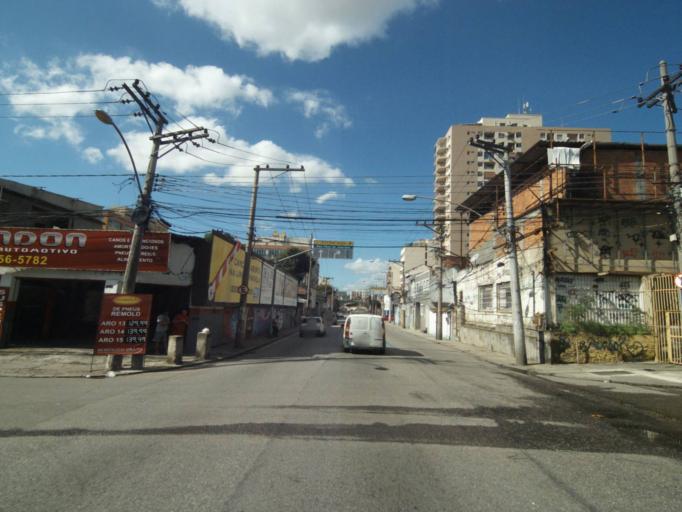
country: BR
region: Rio de Janeiro
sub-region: Rio De Janeiro
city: Rio de Janeiro
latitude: -22.9039
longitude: -43.2600
